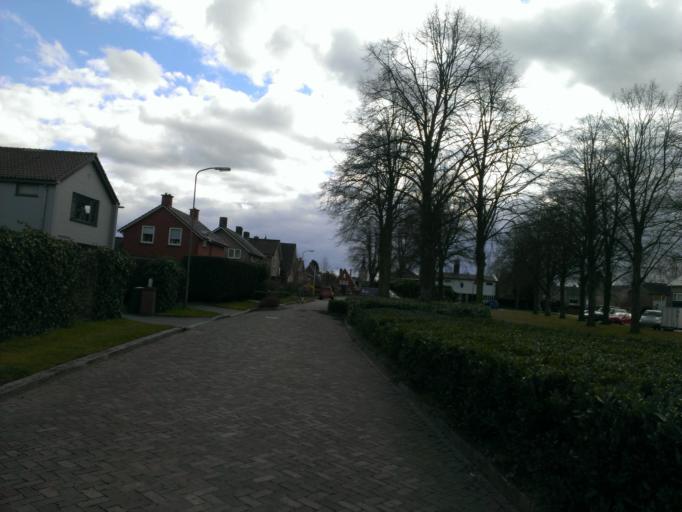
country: NL
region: Gelderland
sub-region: Gemeente Heerde
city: Heerde
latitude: 52.3921
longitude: 6.0433
